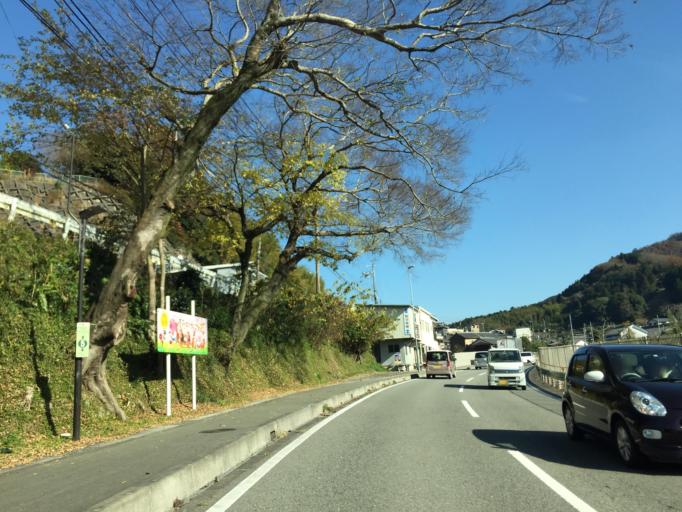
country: JP
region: Wakayama
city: Iwade
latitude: 34.1658
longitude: 135.3019
